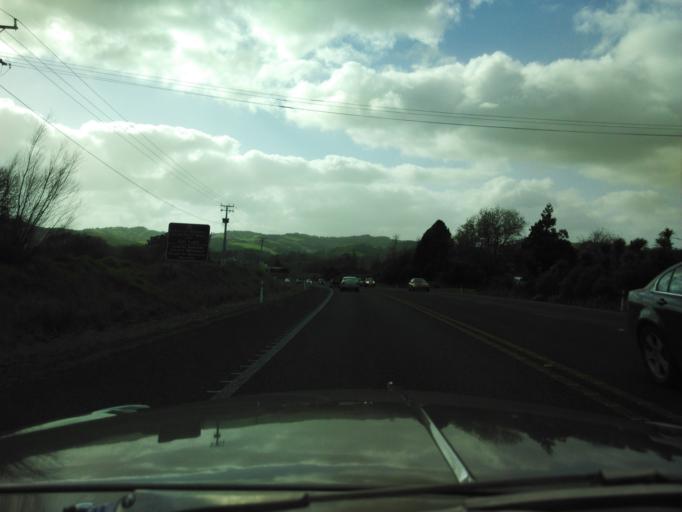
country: NZ
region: Auckland
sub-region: Auckland
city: Wellsford
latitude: -36.2408
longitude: 174.5108
